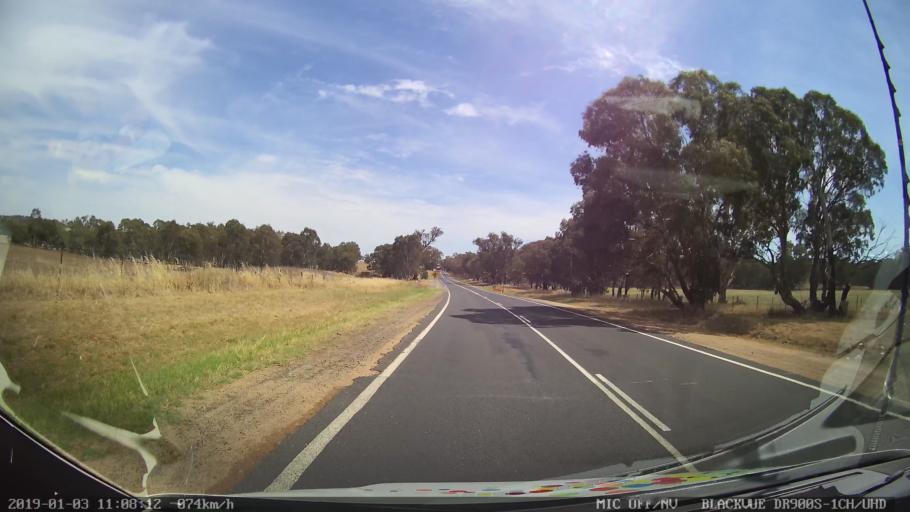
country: AU
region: New South Wales
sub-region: Young
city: Young
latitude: -34.2520
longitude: 148.2581
